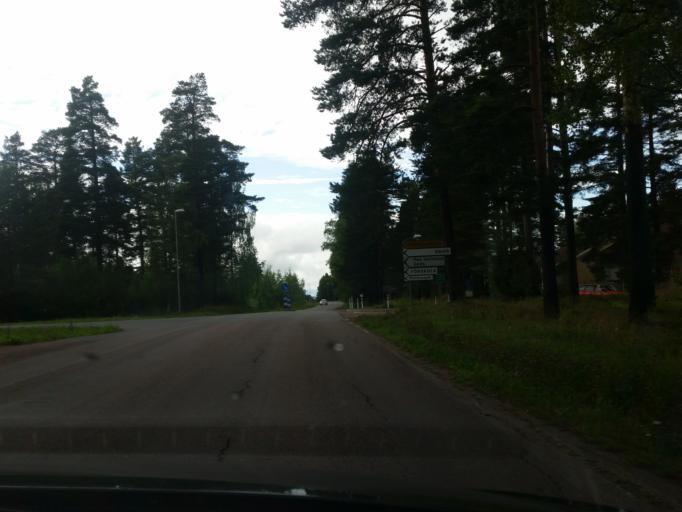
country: SE
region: Dalarna
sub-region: Leksand Municipality
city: Leksand
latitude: 60.7178
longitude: 15.0118
